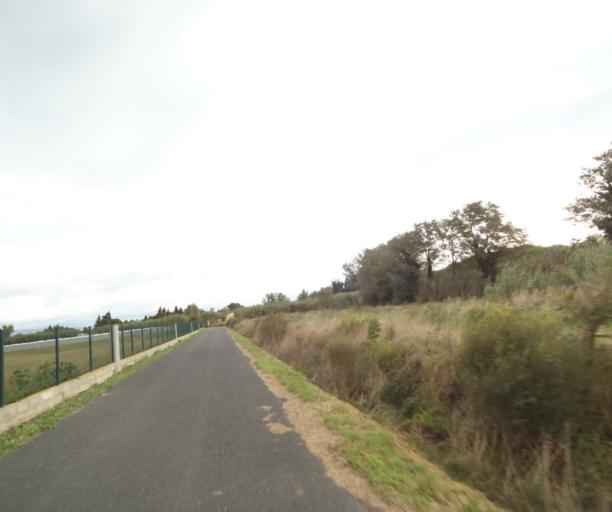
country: FR
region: Languedoc-Roussillon
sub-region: Departement des Pyrenees-Orientales
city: Argelers
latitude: 42.5805
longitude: 3.0296
